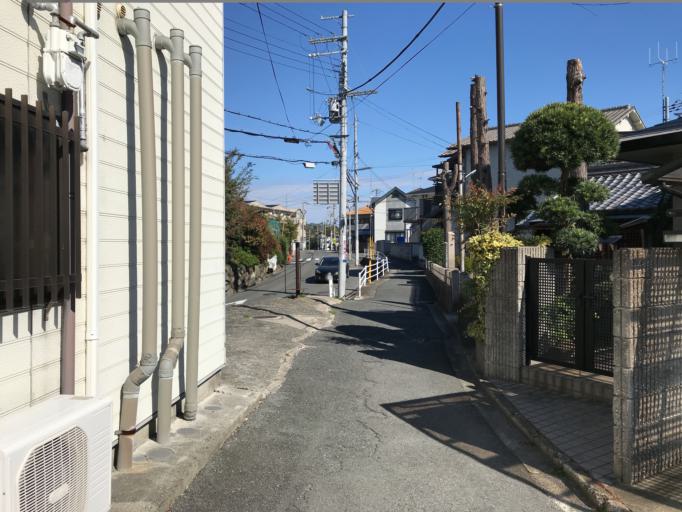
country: JP
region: Osaka
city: Kashihara
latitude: 34.5475
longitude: 135.6091
